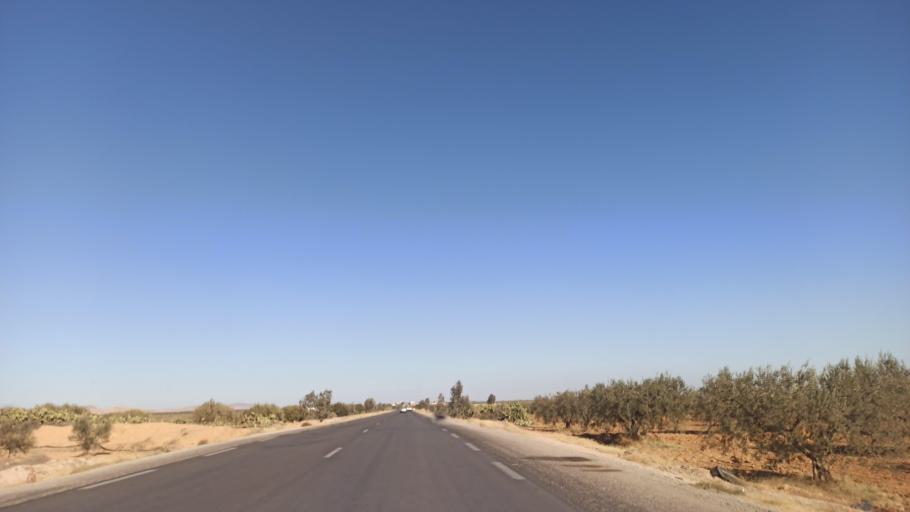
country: TN
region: Sidi Bu Zayd
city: Bi'r al Hufayy
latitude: 34.9540
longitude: 9.2149
